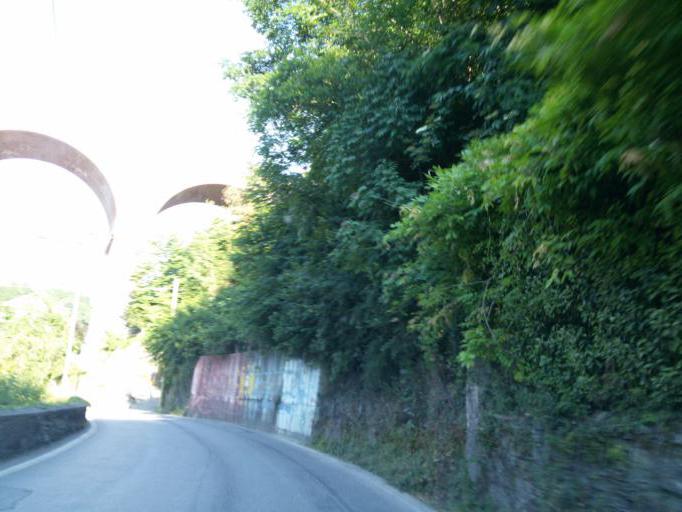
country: IT
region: Liguria
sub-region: Provincia di Genova
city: Santa Marta
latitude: 44.4720
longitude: 8.8917
